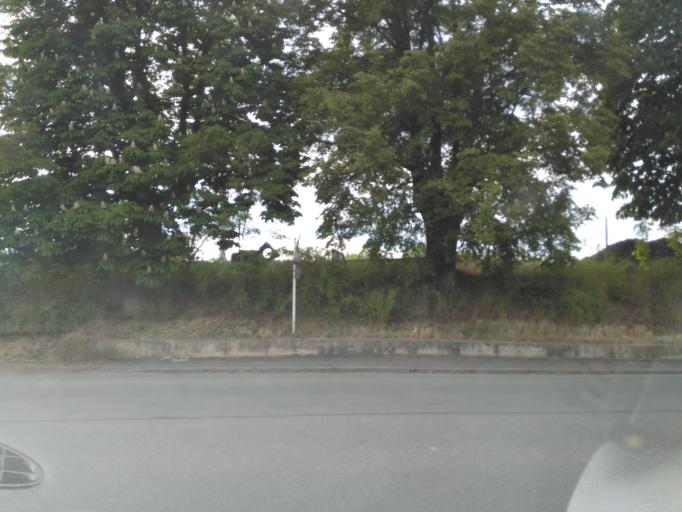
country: CZ
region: Central Bohemia
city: Zdice
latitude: 49.9086
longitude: 13.9841
